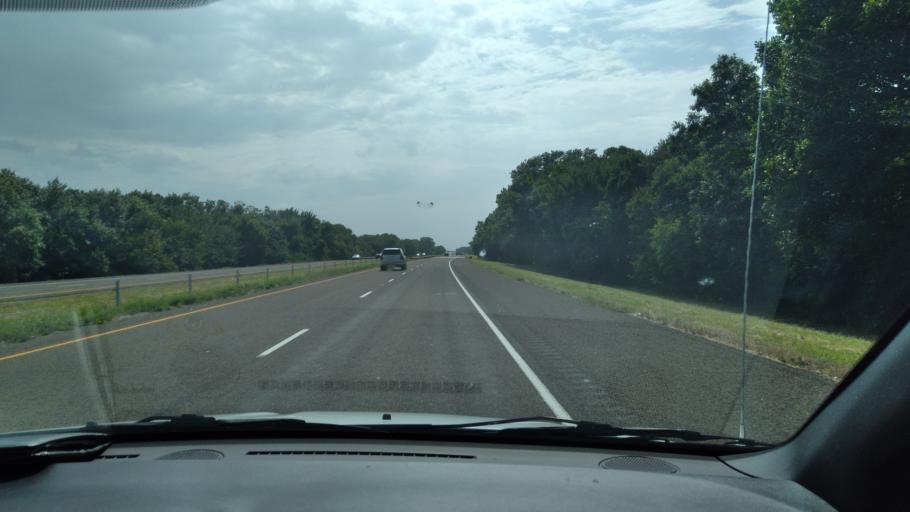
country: US
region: Texas
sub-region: Navarro County
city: Kerens
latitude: 32.1266
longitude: -96.2686
